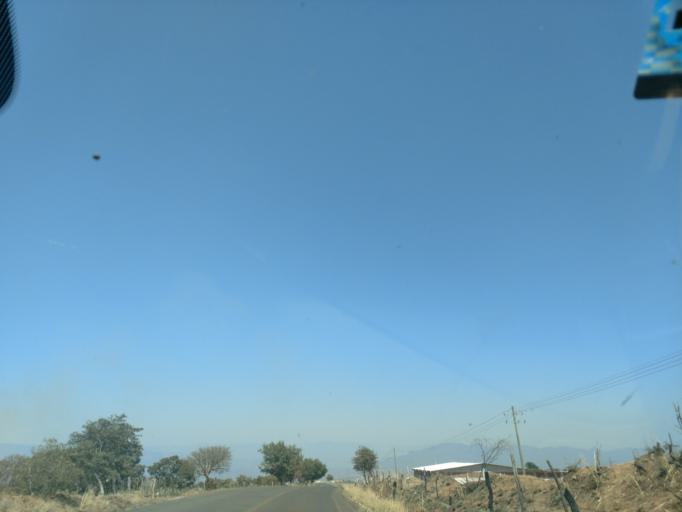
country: MX
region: Nayarit
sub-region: Tepic
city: La Corregidora
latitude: 21.4937
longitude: -104.6936
